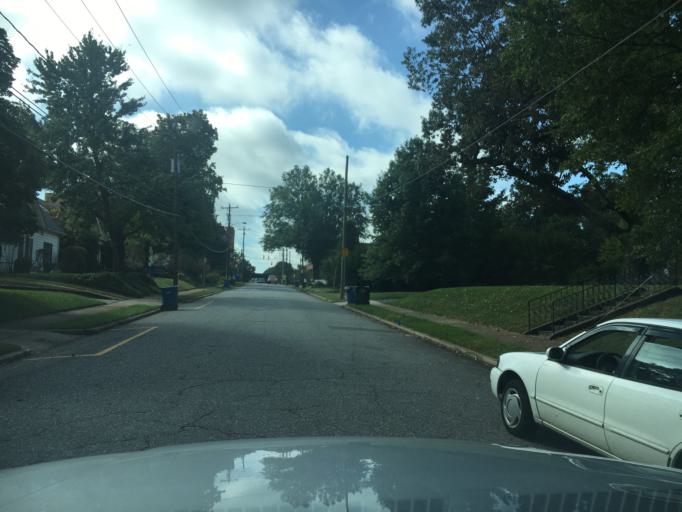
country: US
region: North Carolina
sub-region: Catawba County
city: Hickory
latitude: 35.7398
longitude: -81.3377
